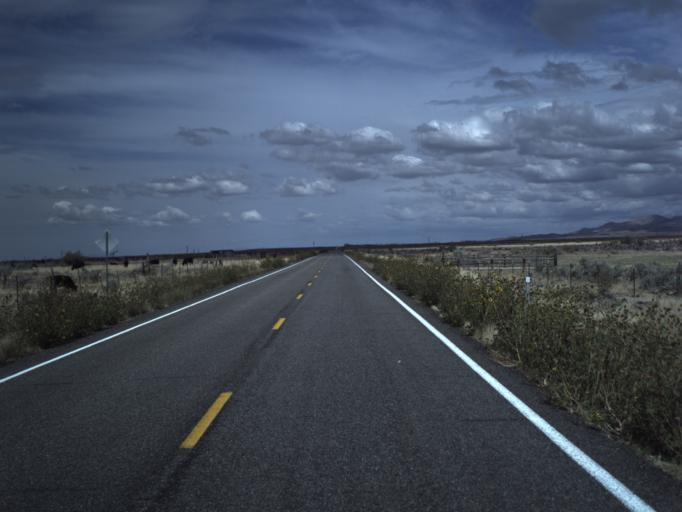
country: US
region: Utah
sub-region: Millard County
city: Fillmore
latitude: 39.1377
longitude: -112.4096
